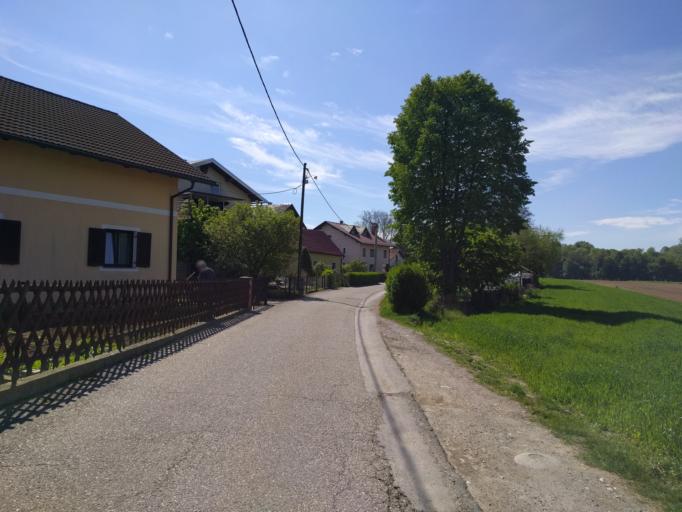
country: SI
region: Miklavz na Dravskem Polju
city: Miklavz na Dravskem Polju
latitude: 46.5332
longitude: 15.6899
